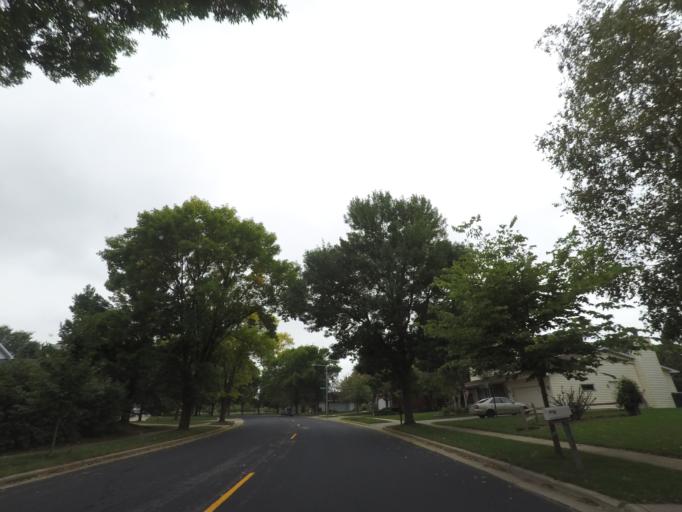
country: US
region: Wisconsin
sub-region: Dane County
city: Middleton
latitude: 43.0813
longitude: -89.5052
